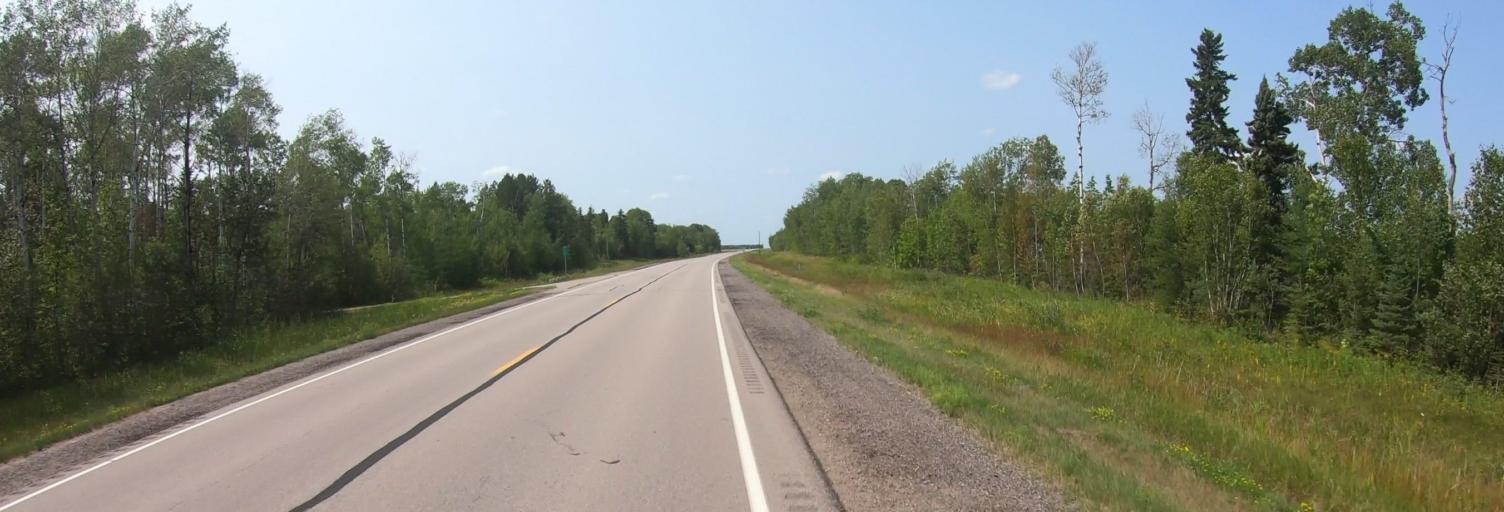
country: US
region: Minnesota
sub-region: Lake of the Woods County
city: Baudette
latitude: 48.7152
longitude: -94.7307
